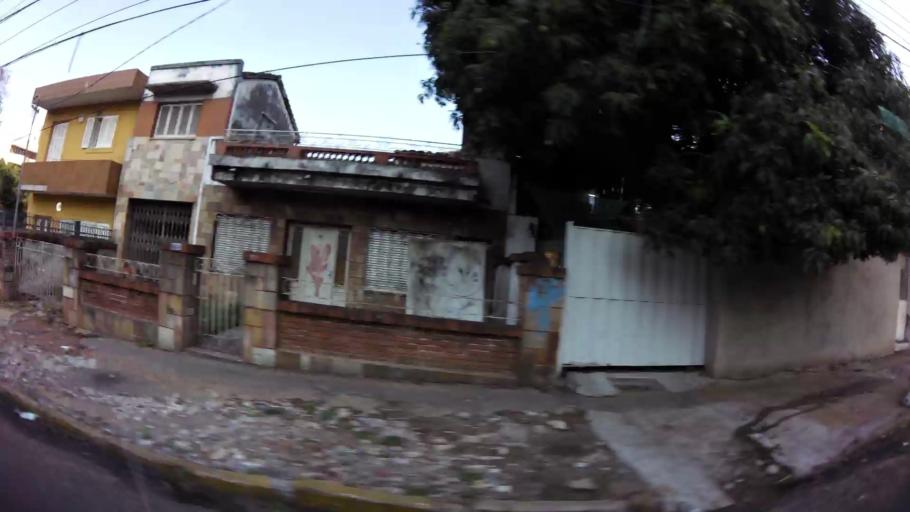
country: PY
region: Asuncion
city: Asuncion
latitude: -25.2935
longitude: -57.6221
